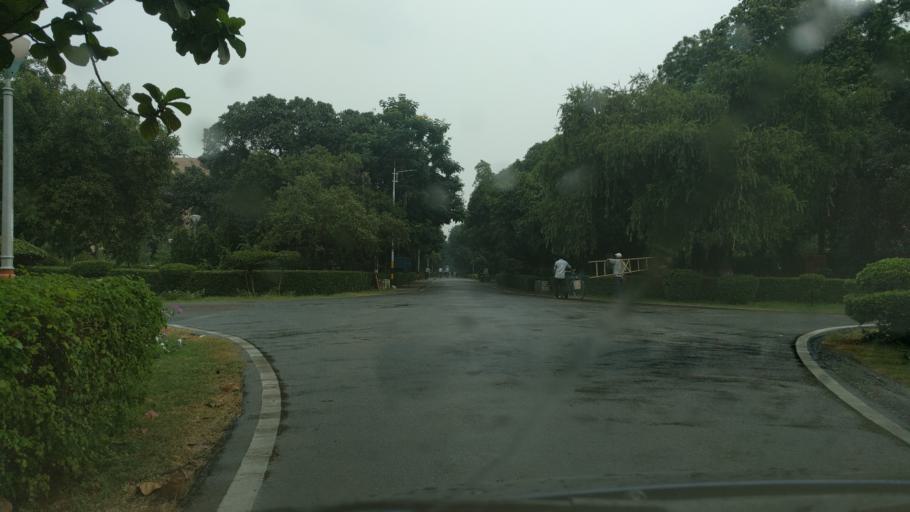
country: IN
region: NCT
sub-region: Central Delhi
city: Karol Bagh
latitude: 28.6392
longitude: 77.1670
